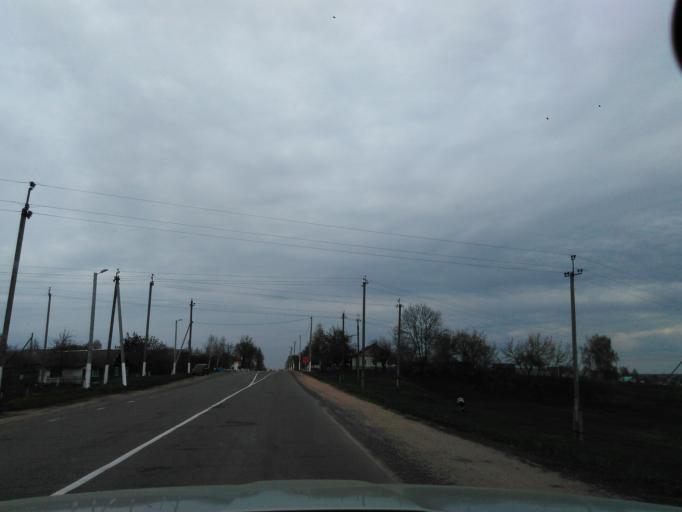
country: BY
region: Vitebsk
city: Chashniki
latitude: 54.8419
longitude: 29.1775
